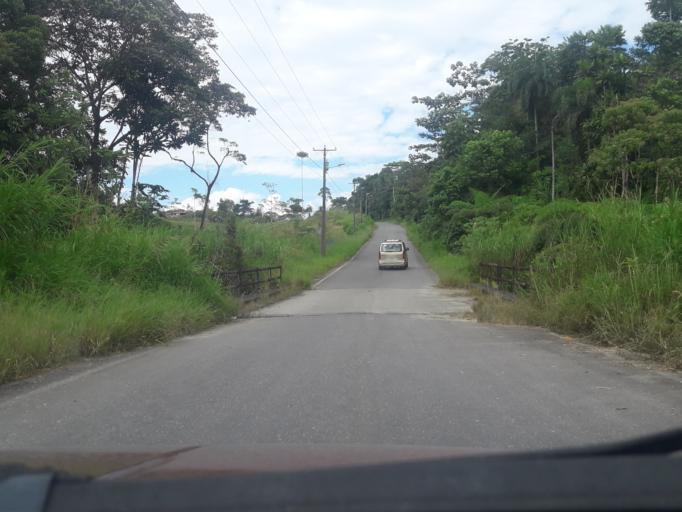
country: EC
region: Napo
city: Tena
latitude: -1.0335
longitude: -77.8889
